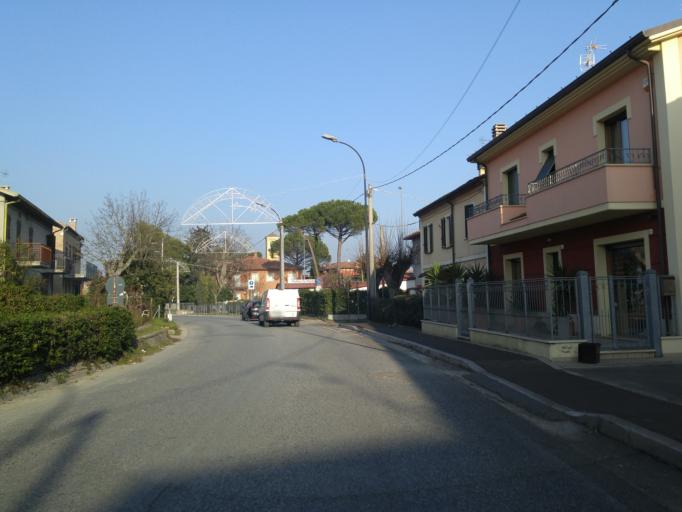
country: IT
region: The Marches
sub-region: Provincia di Pesaro e Urbino
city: Lucrezia
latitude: 43.7725
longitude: 12.9348
